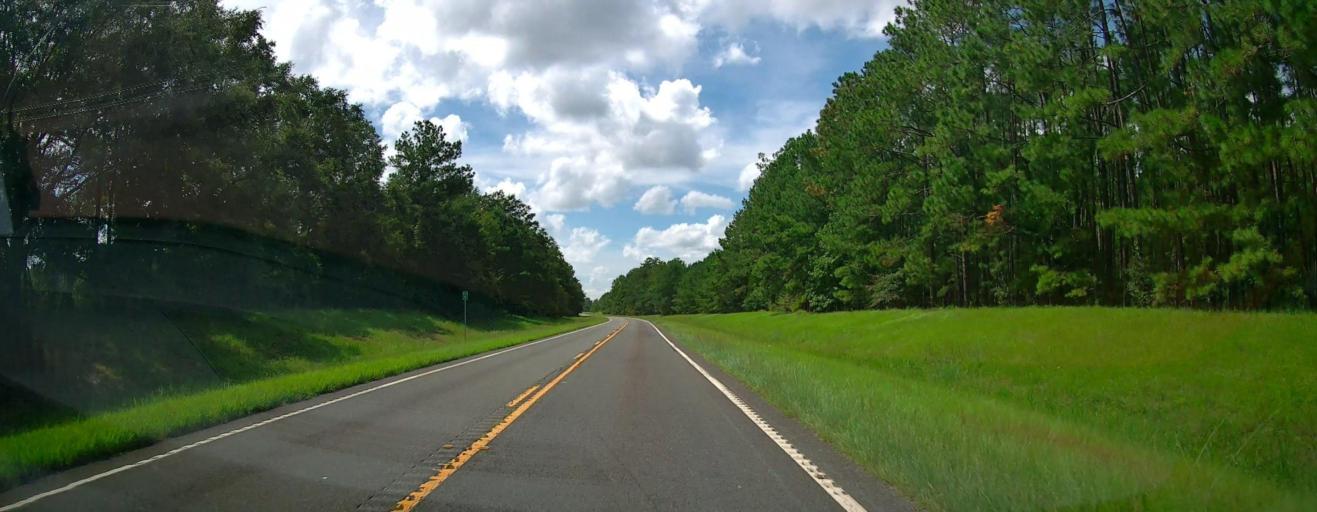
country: US
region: Georgia
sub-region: Macon County
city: Marshallville
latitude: 32.4337
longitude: -84.0432
